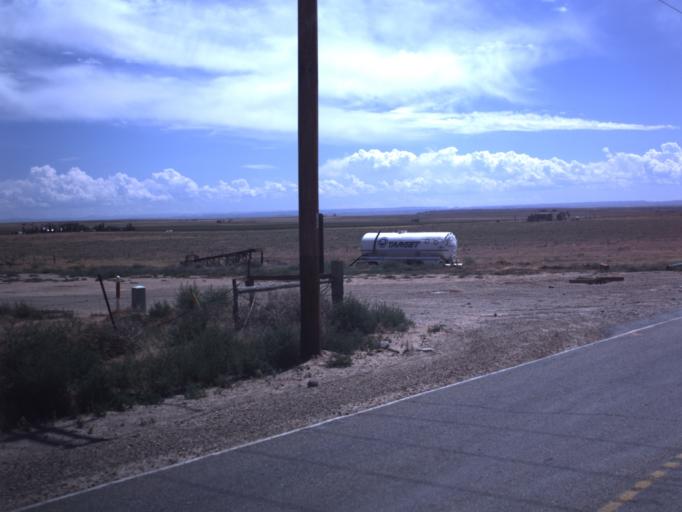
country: US
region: Utah
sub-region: Uintah County
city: Naples
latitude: 40.1741
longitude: -109.6645
